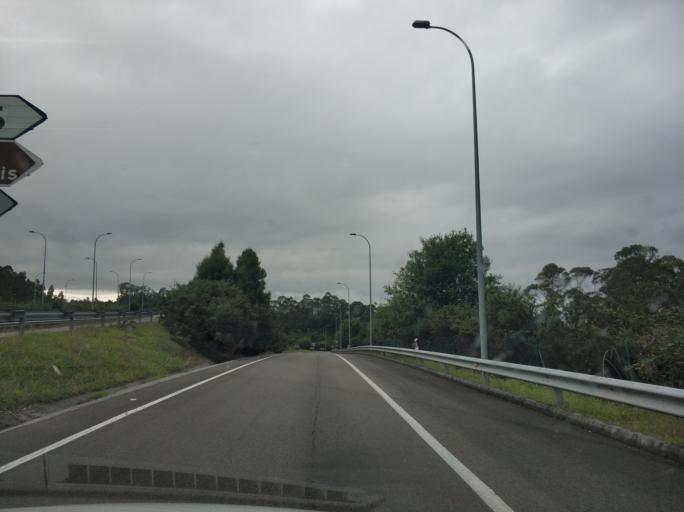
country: ES
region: Galicia
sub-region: Provincia de Lugo
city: Barreiros
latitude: 43.5370
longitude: -7.1489
